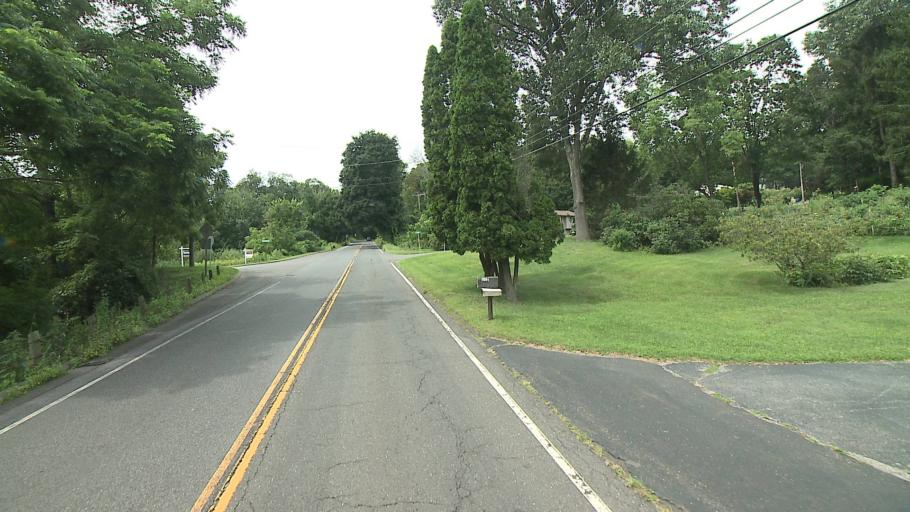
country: US
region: Connecticut
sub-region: Fairfield County
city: Newtown
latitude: 41.4732
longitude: -73.3561
